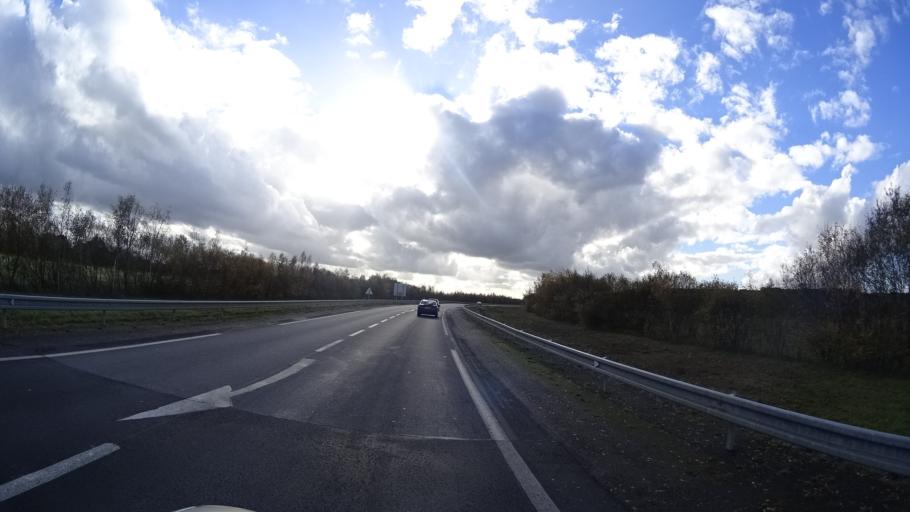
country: FR
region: Brittany
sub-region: Departement d'Ille-et-Vilaine
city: Redon
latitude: 47.6474
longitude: -2.0977
